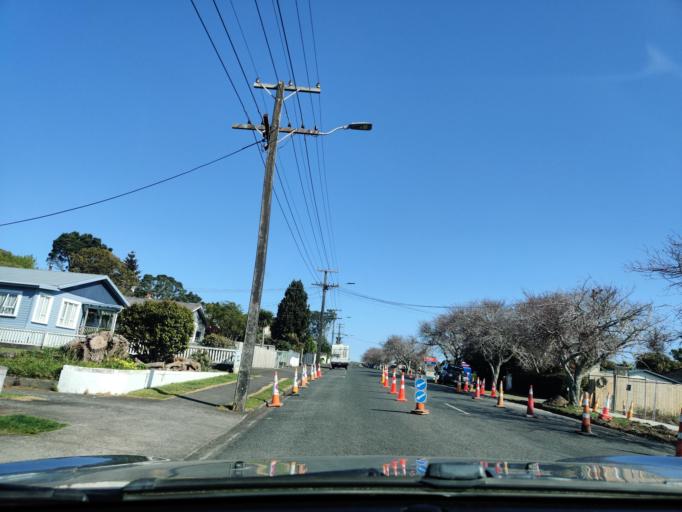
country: NZ
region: Taranaki
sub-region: New Plymouth District
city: New Plymouth
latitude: -39.0710
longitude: 174.0573
